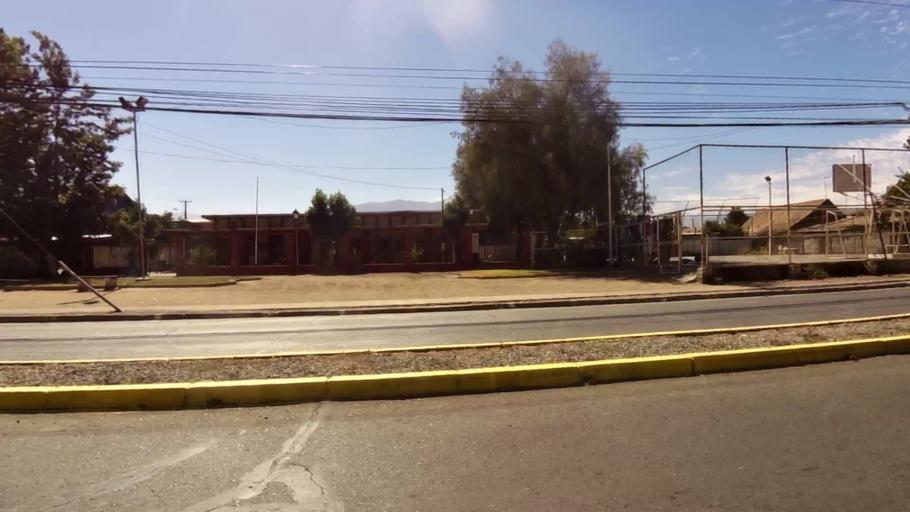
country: CL
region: O'Higgins
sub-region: Provincia de Cachapoal
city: Graneros
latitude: -33.9704
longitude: -70.7121
